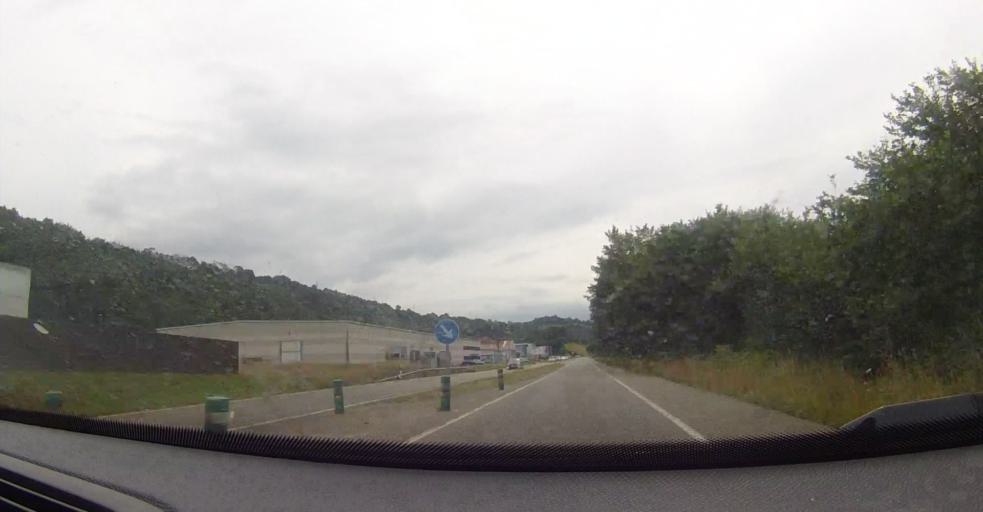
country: ES
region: Asturias
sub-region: Province of Asturias
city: Pilona
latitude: 43.3521
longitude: -5.3244
